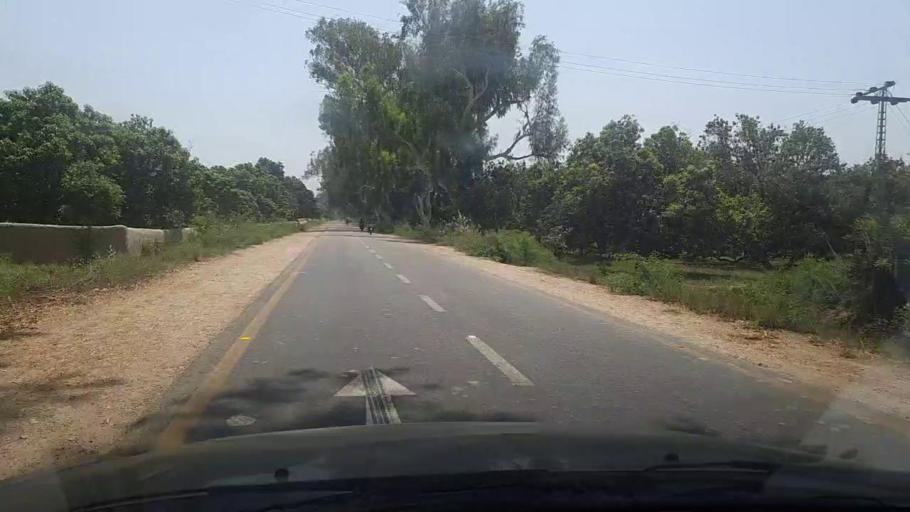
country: PK
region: Sindh
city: Tando Jam
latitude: 25.3500
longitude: 68.5101
